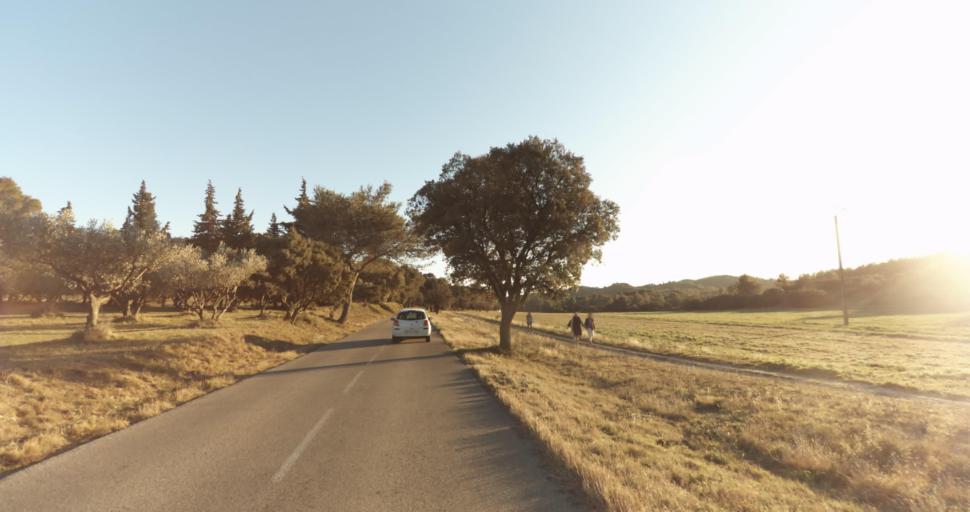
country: FR
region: Provence-Alpes-Cote d'Azur
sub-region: Departement des Bouches-du-Rhone
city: Barbentane
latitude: 43.8714
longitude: 4.7299
